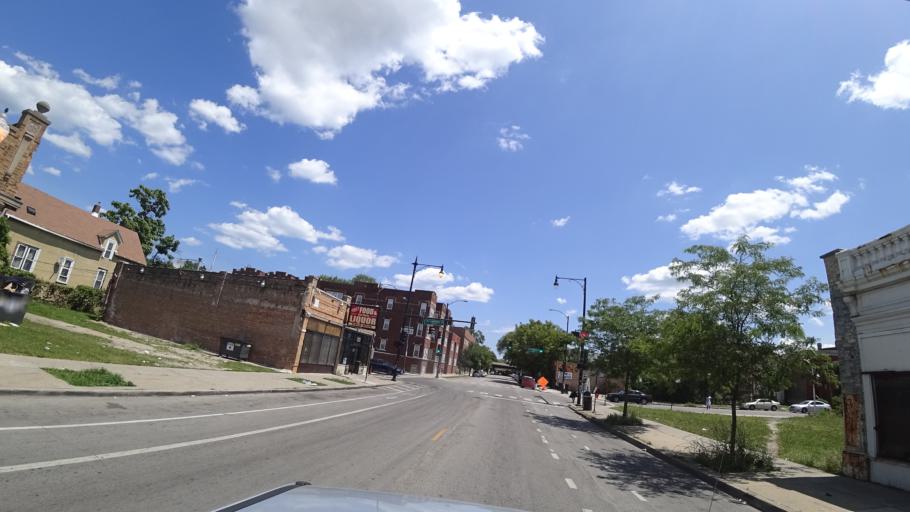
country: US
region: Illinois
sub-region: Cook County
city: Chicago
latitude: 41.7658
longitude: -87.6109
